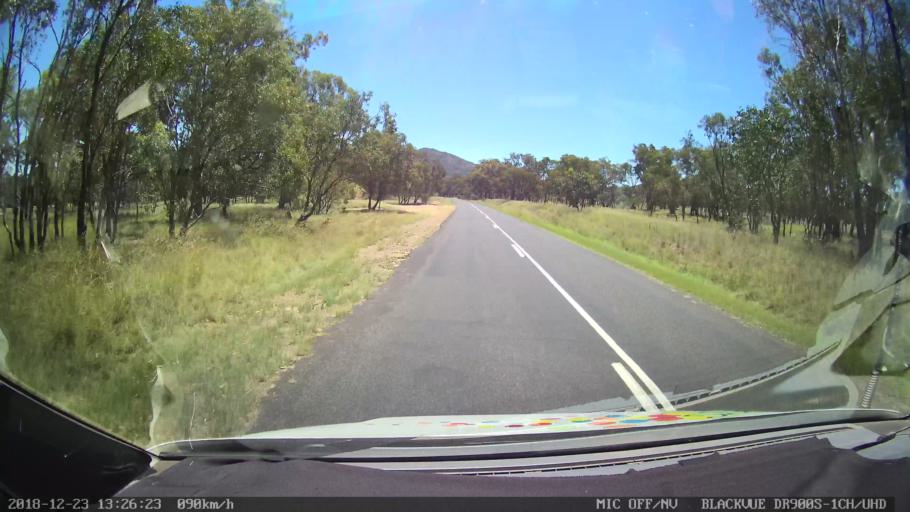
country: AU
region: New South Wales
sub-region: Armidale Dumaresq
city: Armidale
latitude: -30.4680
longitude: 151.3699
